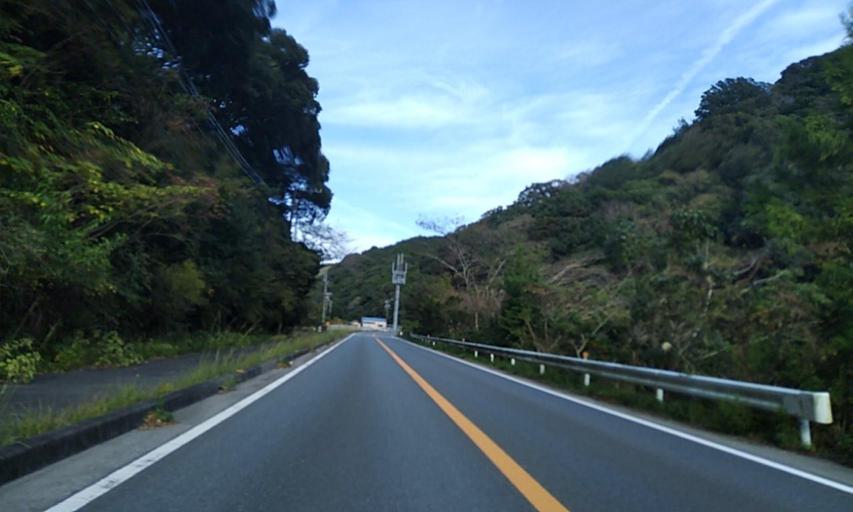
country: JP
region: Mie
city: Ise
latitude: 34.3557
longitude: 136.7440
